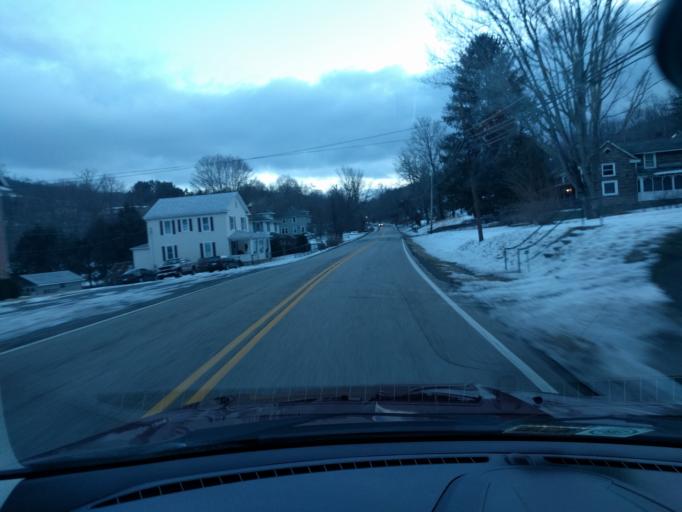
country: US
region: Virginia
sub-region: Bath County
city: Warm Springs
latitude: 37.9630
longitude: -79.8605
